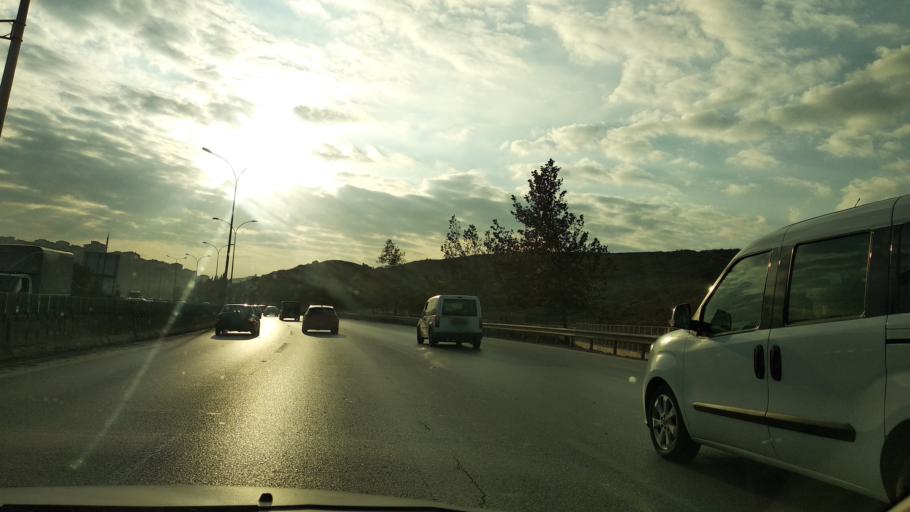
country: TR
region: Istanbul
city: Icmeler
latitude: 40.8773
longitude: 29.3052
